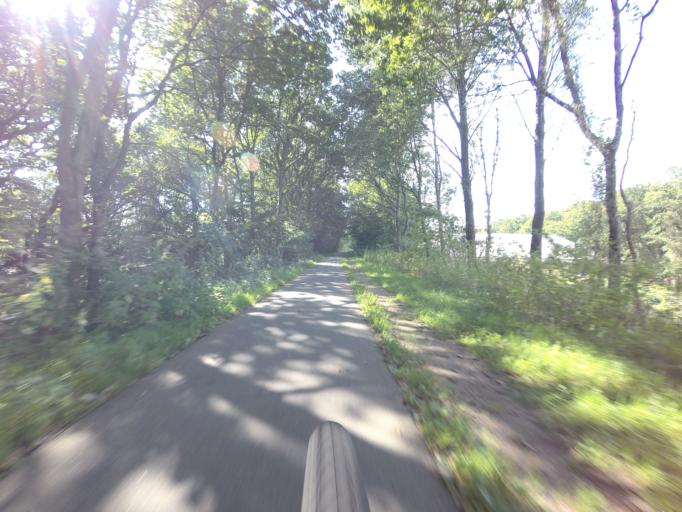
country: DK
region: Central Jutland
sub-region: Viborg Kommune
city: Viborg
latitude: 56.4019
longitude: 9.3541
